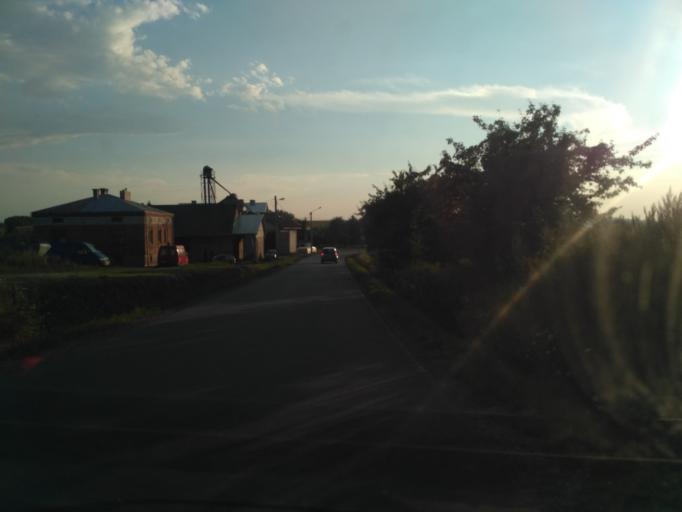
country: PL
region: Subcarpathian Voivodeship
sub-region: Powiat krosnienski
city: Kroscienko Wyzne
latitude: 49.7052
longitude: 21.8349
